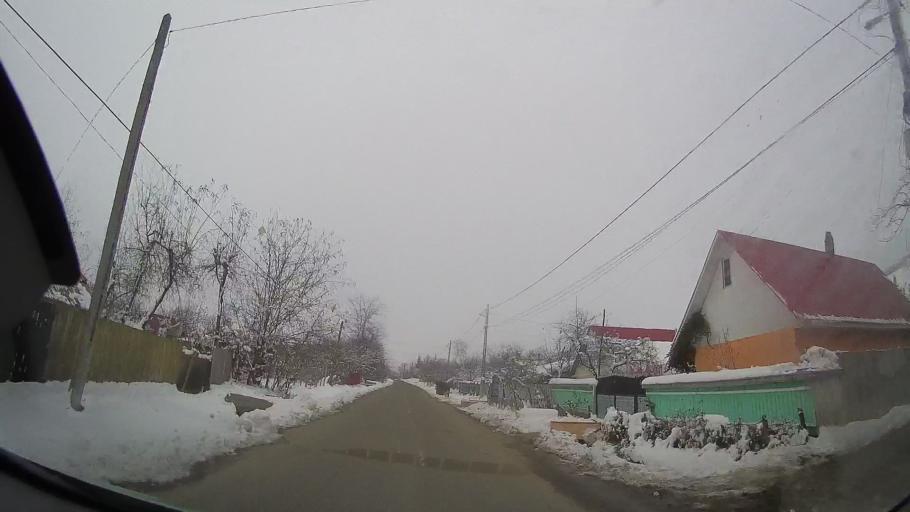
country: RO
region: Neamt
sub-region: Comuna Bozieni
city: Bozieni
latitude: 46.8300
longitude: 27.1806
